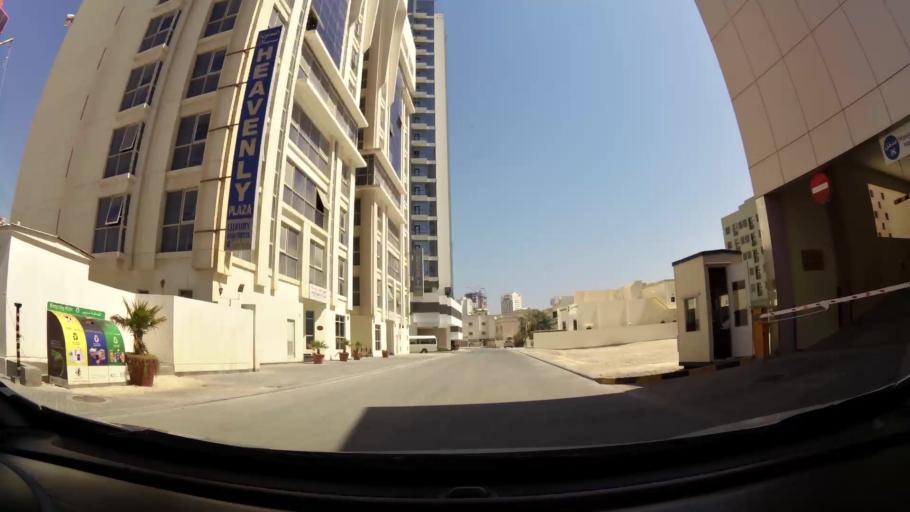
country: BH
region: Manama
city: Manama
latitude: 26.2143
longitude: 50.6106
